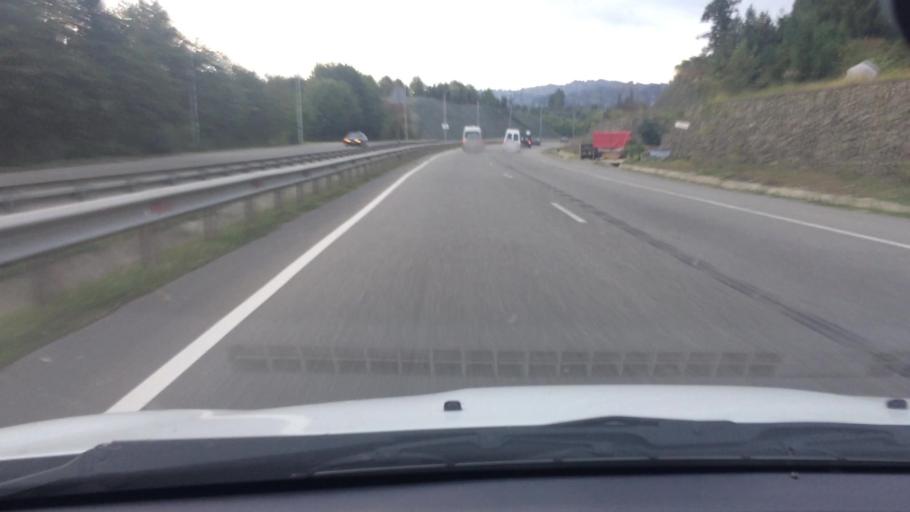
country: GE
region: Ajaria
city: Makhinjauri
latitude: 41.6970
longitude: 41.7276
